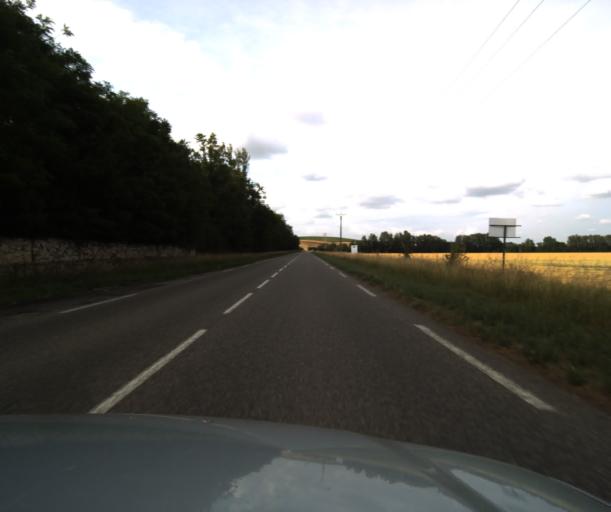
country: FR
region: Midi-Pyrenees
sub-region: Departement du Tarn-et-Garonne
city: Beaumont-de-Lomagne
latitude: 43.8608
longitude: 0.9511
